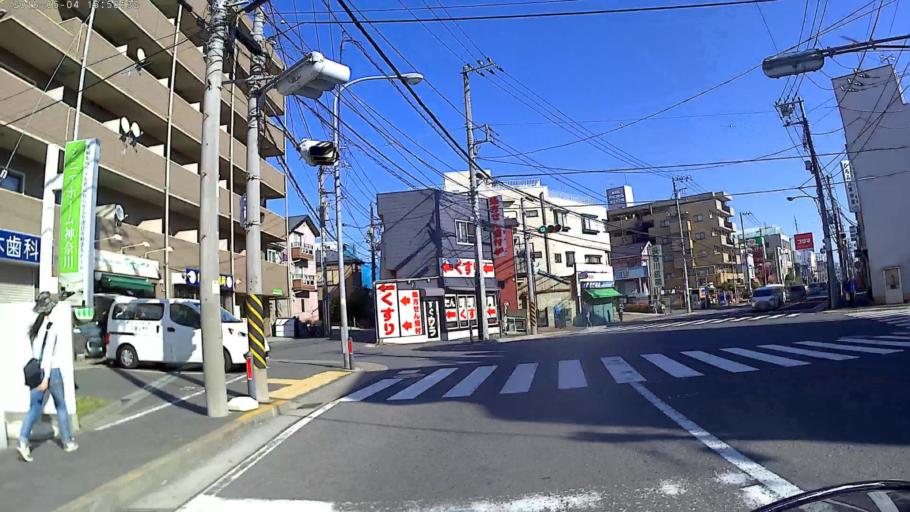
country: JP
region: Kanagawa
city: Yokohama
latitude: 35.4953
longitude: 139.6476
